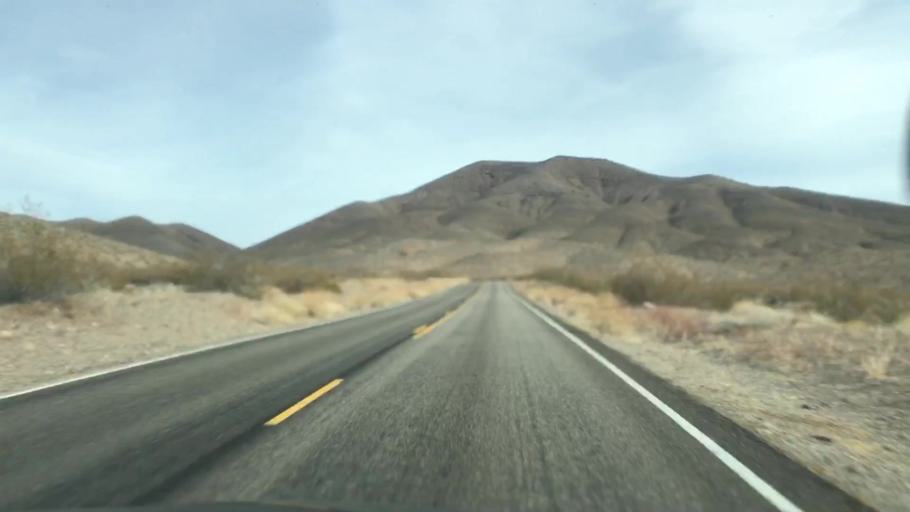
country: US
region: Nevada
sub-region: Nye County
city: Beatty
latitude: 36.7577
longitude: -116.9324
